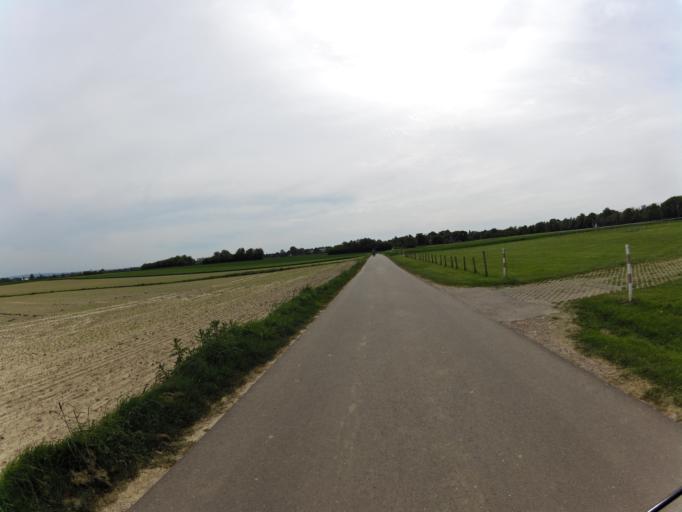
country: DE
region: North Rhine-Westphalia
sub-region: Regierungsbezirk Koln
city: Wurselen
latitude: 50.8331
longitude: 6.1445
